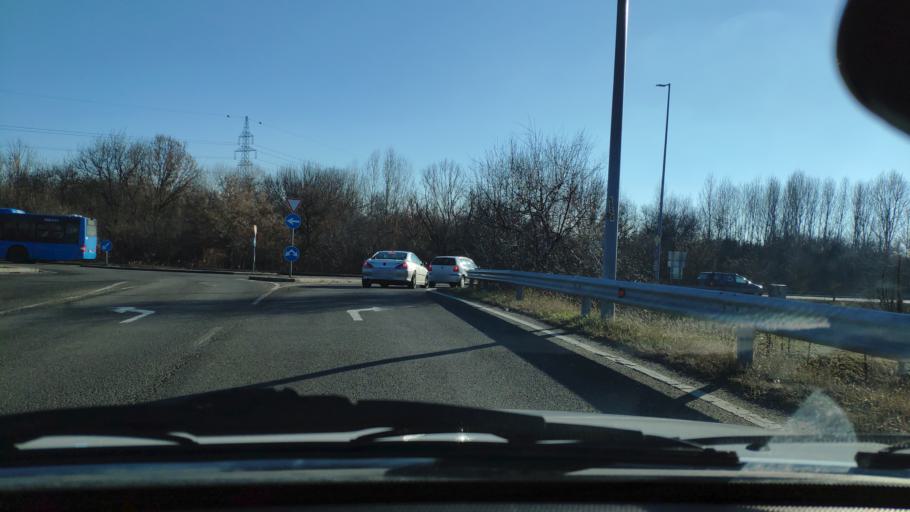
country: HU
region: Budapest
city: Budapest XIX. keruelet
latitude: 47.4235
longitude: 19.1485
